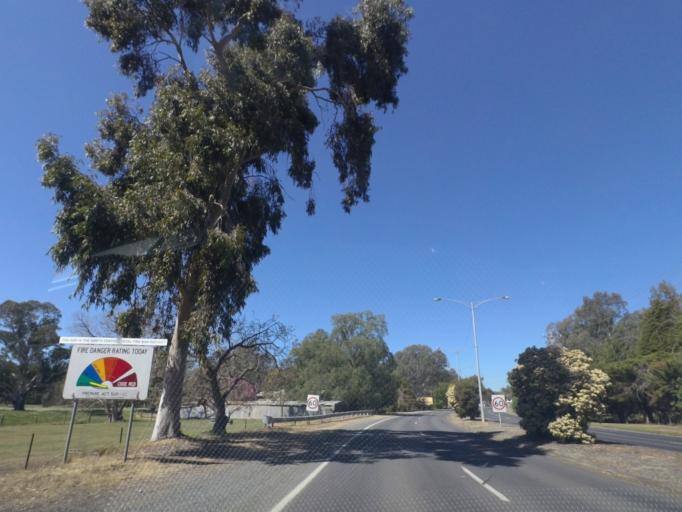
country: AU
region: Victoria
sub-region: Murrindindi
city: Kinglake West
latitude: -37.0213
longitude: 145.1193
